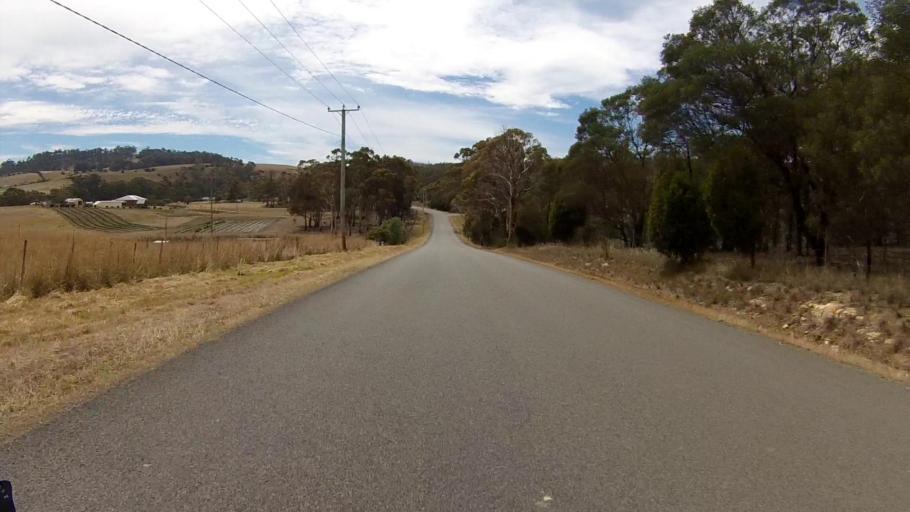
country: AU
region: Tasmania
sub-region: Sorell
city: Sorell
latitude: -42.8052
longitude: 147.6405
